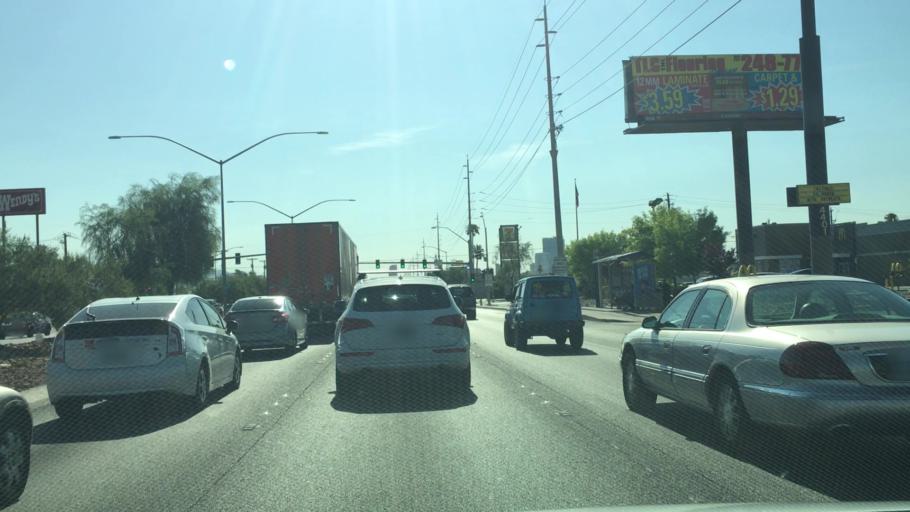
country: US
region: Nevada
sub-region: Clark County
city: Spring Valley
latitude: 36.1444
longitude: -115.2012
